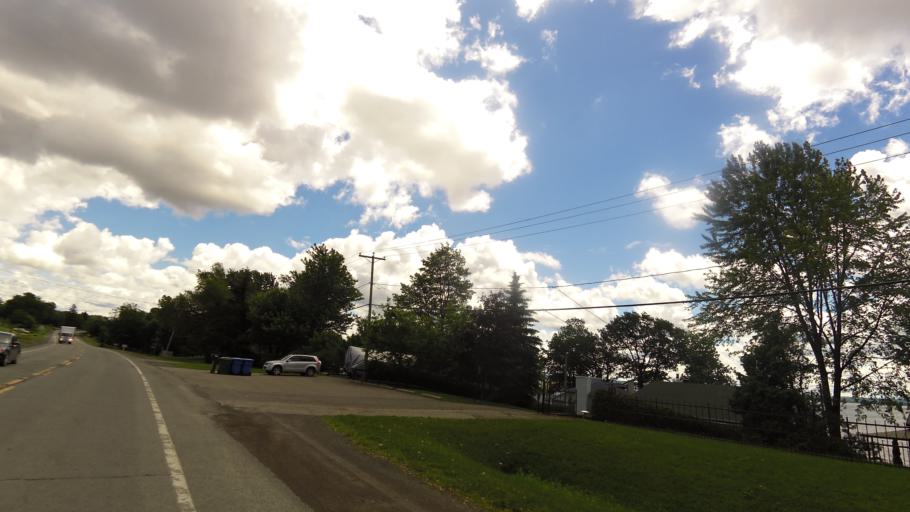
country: CA
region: Quebec
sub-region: Monteregie
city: Rigaud
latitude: 45.5307
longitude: -74.2370
